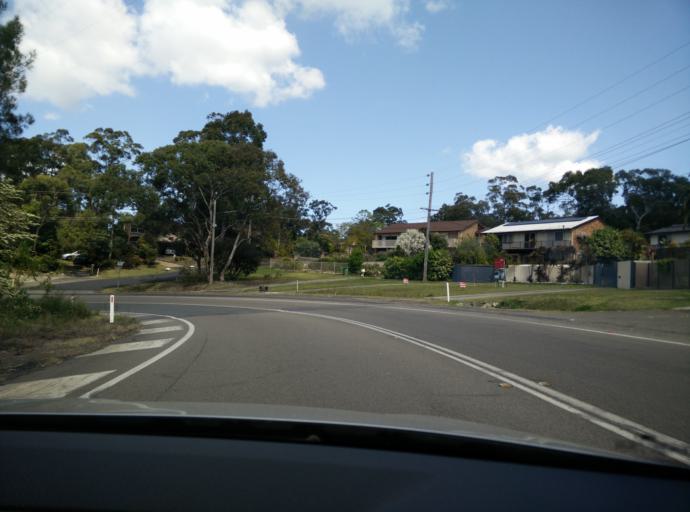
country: AU
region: New South Wales
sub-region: Gosford Shire
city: Blackwall
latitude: -33.4926
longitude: 151.2988
